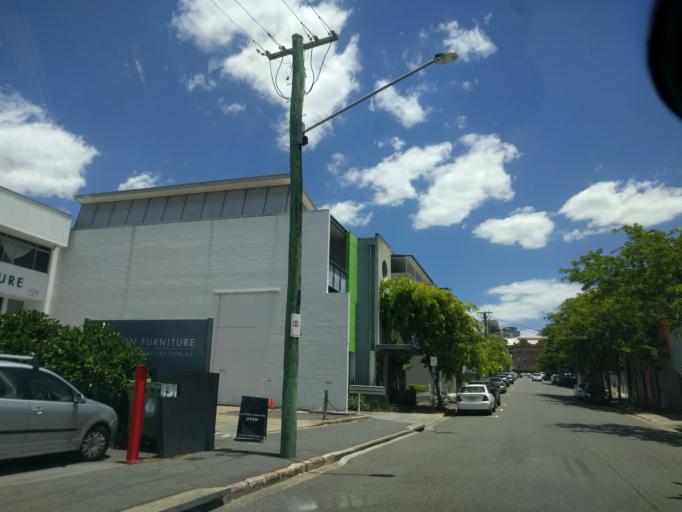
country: AU
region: Queensland
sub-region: Brisbane
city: Fortitude Valley
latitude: -27.4580
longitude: 153.0394
